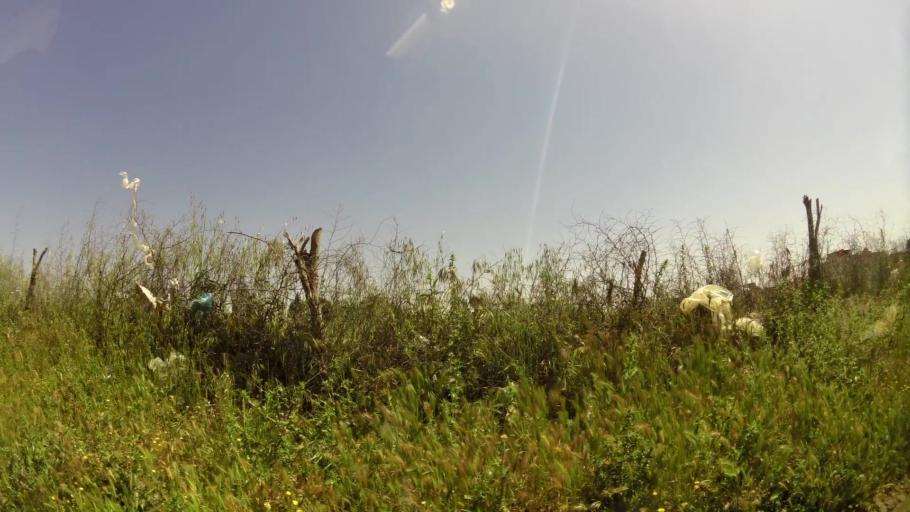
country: MA
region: Rabat-Sale-Zemmour-Zaer
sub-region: Khemisset
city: Khemisset
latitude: 33.8100
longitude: -6.0862
